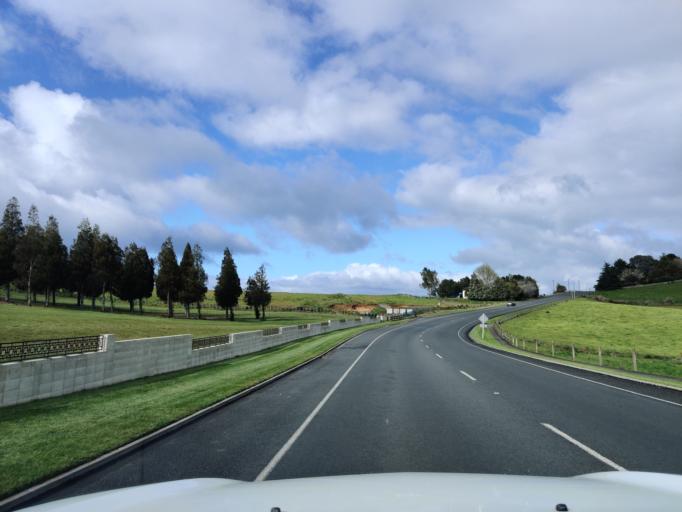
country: NZ
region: Waikato
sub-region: Hamilton City
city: Hamilton
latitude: -37.8272
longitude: 175.2228
